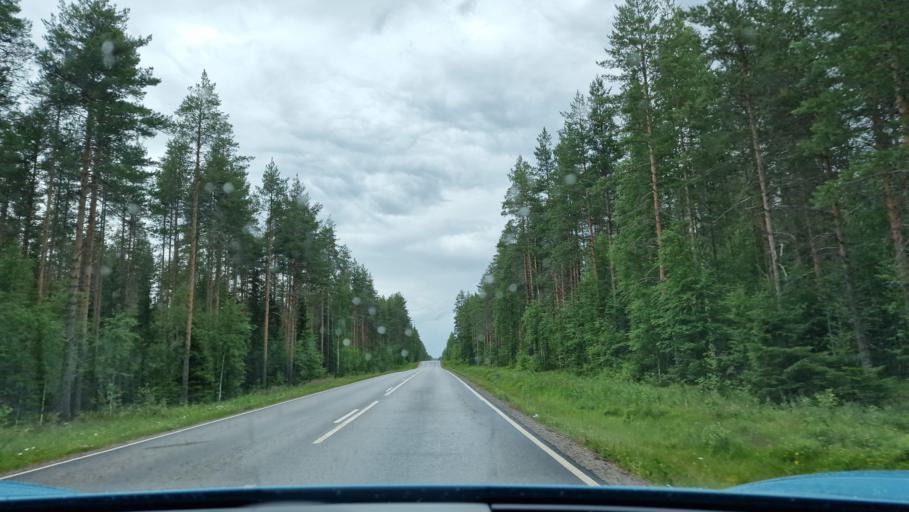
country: FI
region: Central Finland
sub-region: Saarijaervi-Viitasaari
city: Pylkoenmaeki
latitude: 62.6244
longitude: 24.5805
